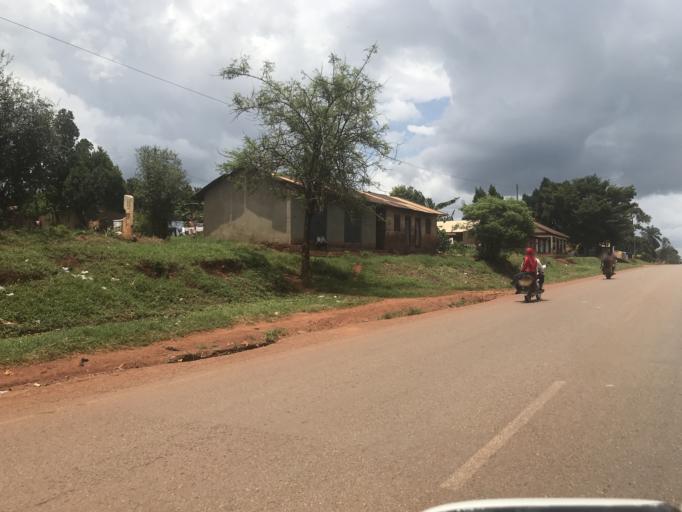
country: UG
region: Eastern Region
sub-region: Jinja District
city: Bugembe
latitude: 0.4700
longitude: 33.2481
